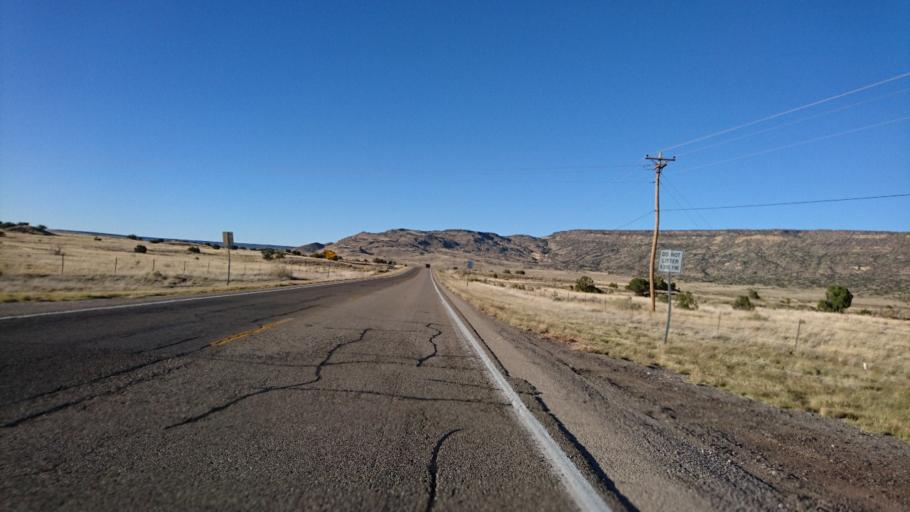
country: US
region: New Mexico
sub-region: Cibola County
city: Grants
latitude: 35.0889
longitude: -107.7701
